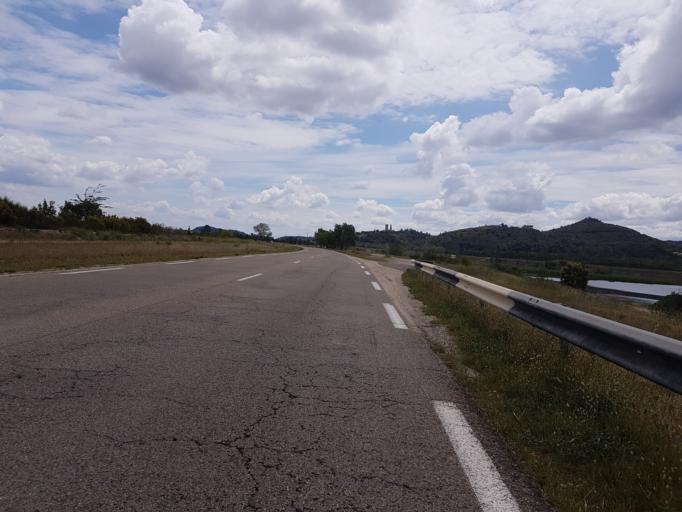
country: FR
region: Languedoc-Roussillon
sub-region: Departement du Gard
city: Vallabregues
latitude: 43.8541
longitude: 4.6174
